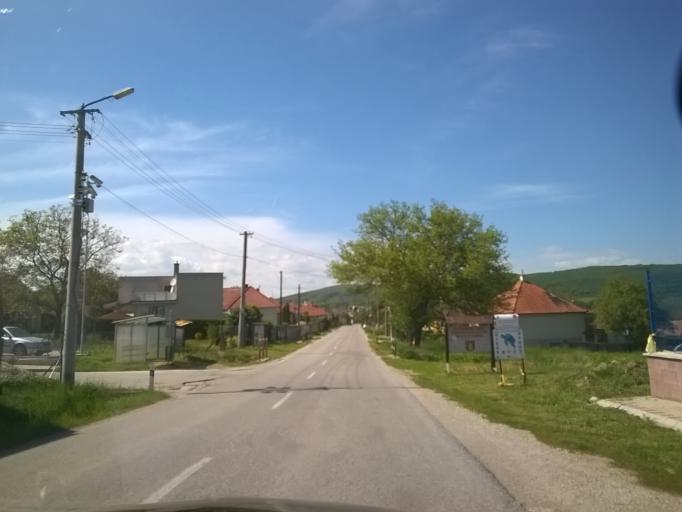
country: SK
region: Nitriansky
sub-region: Okres Nitra
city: Nitra
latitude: 48.3714
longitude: 18.1817
